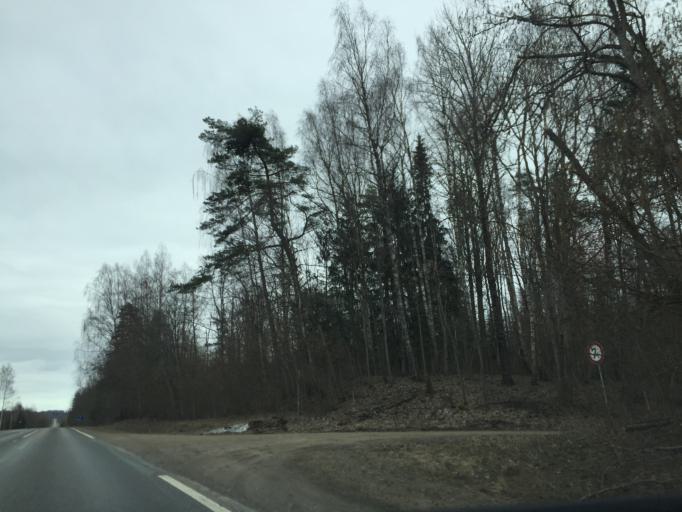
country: LV
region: Kraslavas Rajons
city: Kraslava
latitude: 55.9132
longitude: 27.0456
